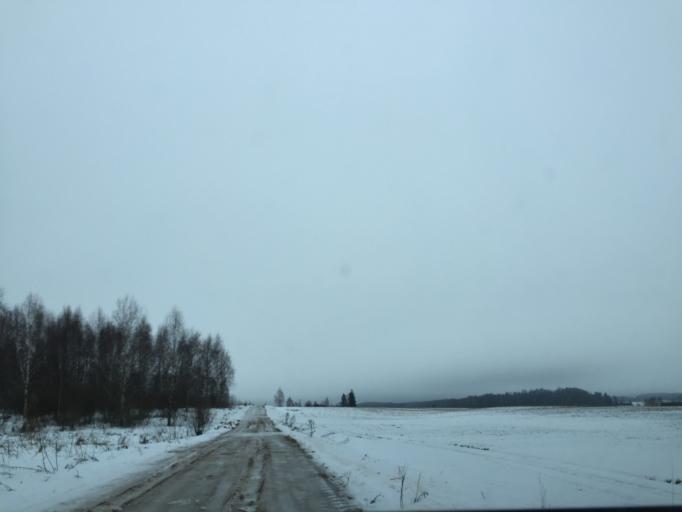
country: LV
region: Krimulda
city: Ragana
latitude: 57.1599
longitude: 24.7576
